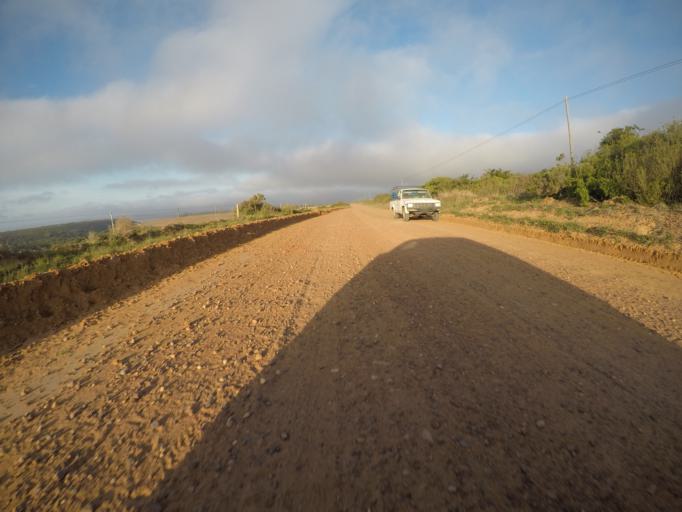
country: ZA
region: Western Cape
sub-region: Eden District Municipality
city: Mossel Bay
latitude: -34.1431
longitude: 22.0252
